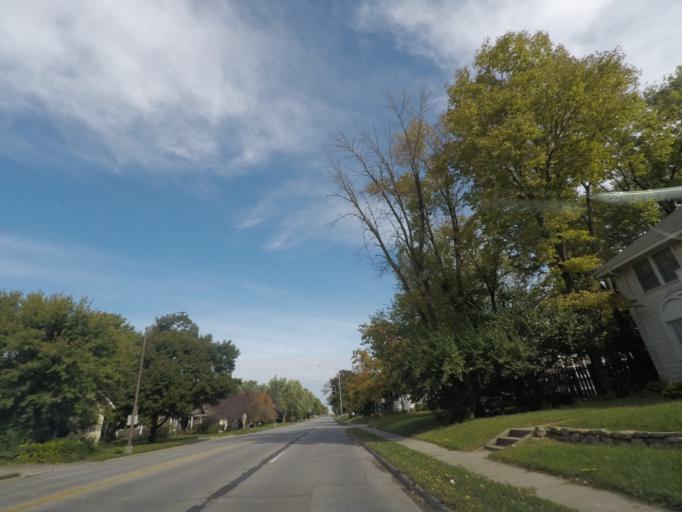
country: US
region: Iowa
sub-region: Story County
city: Ames
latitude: 42.0308
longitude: -93.6203
